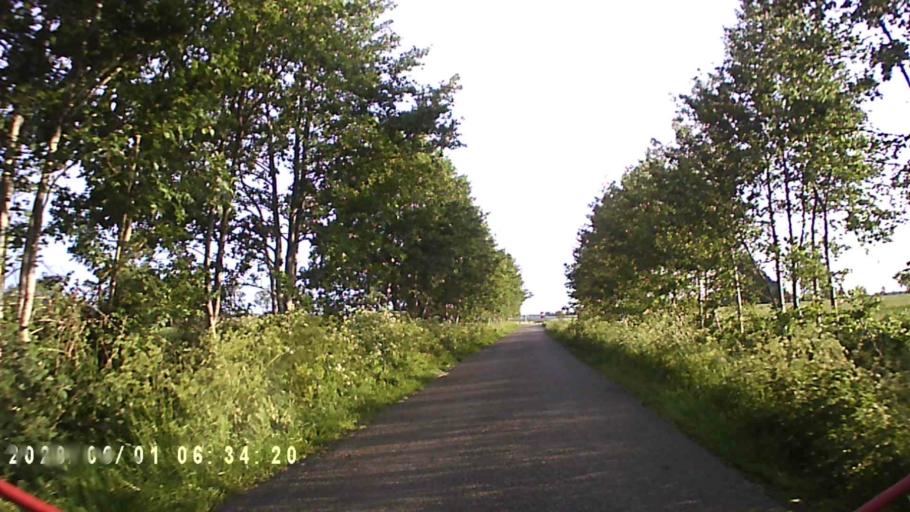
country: NL
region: Friesland
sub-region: Gemeente Kollumerland en Nieuwkruisland
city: Kollum
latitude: 53.2791
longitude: 6.1664
